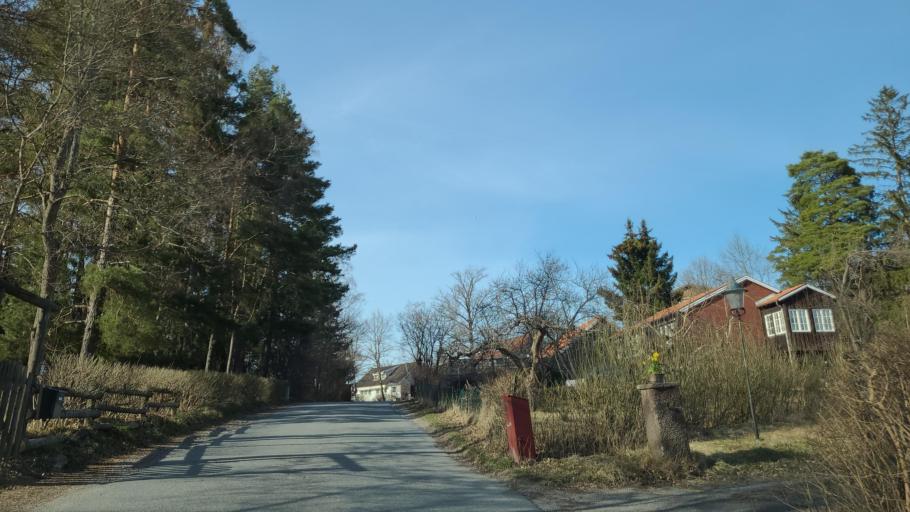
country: SE
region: Stockholm
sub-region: Ekero Kommun
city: Ekeroe
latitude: 59.2850
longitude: 17.7707
